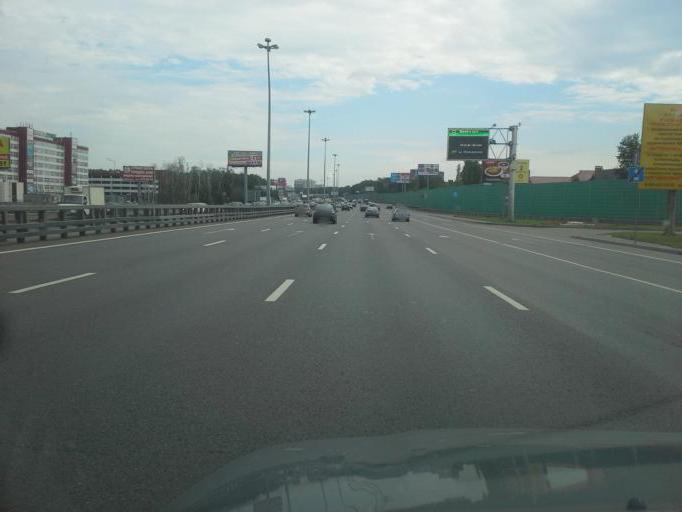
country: RU
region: Moskovskaya
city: Mosrentgen
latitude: 55.6311
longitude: 37.4390
